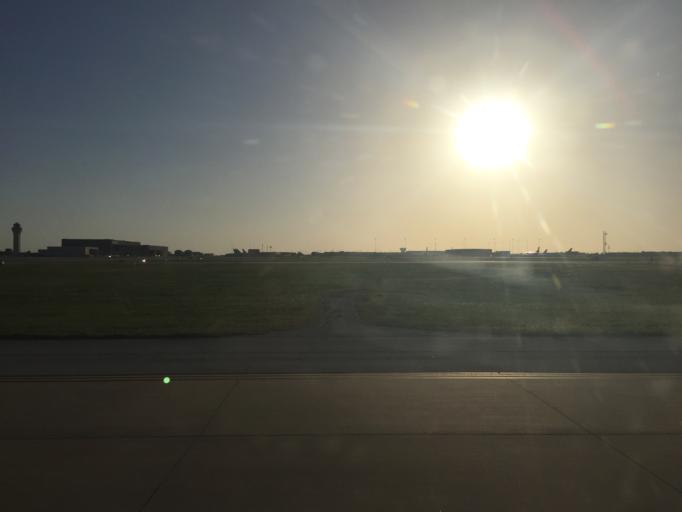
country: US
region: Texas
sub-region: Tarrant County
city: Grapevine
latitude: 32.9114
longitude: -97.0489
